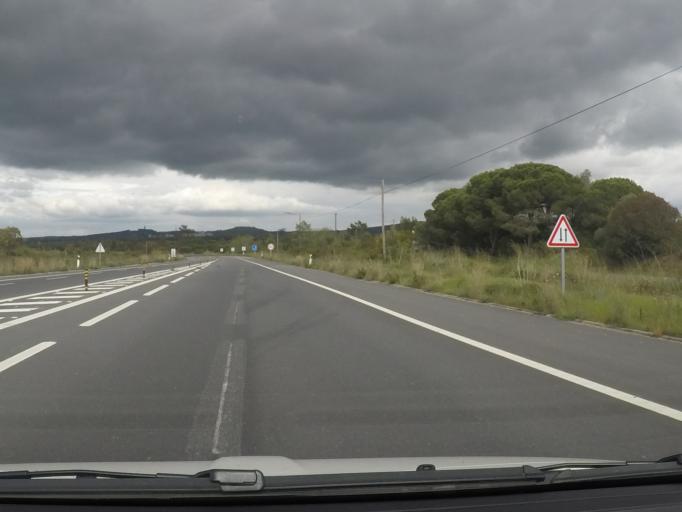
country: PT
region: Setubal
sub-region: Santiago do Cacem
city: Santo Andre
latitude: 37.9991
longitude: -8.7475
